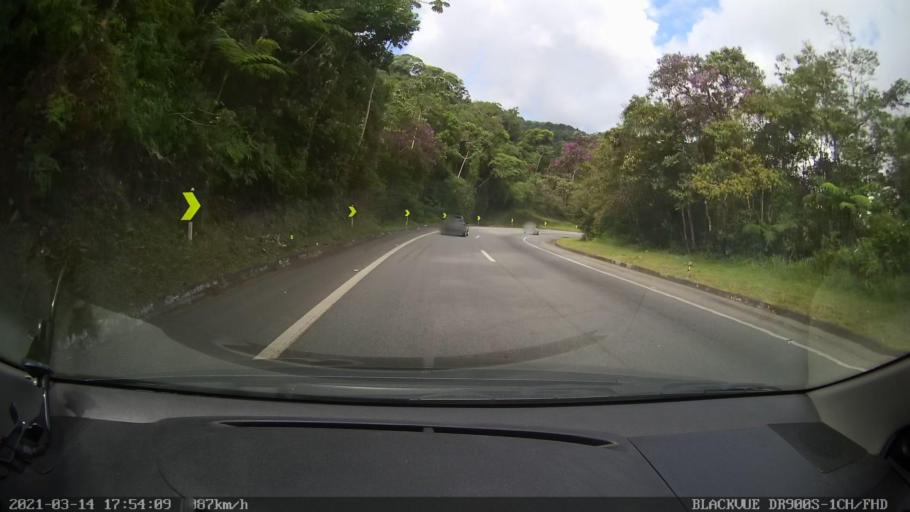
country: BR
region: Rio de Janeiro
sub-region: Petropolis
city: Petropolis
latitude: -22.4850
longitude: -43.2287
